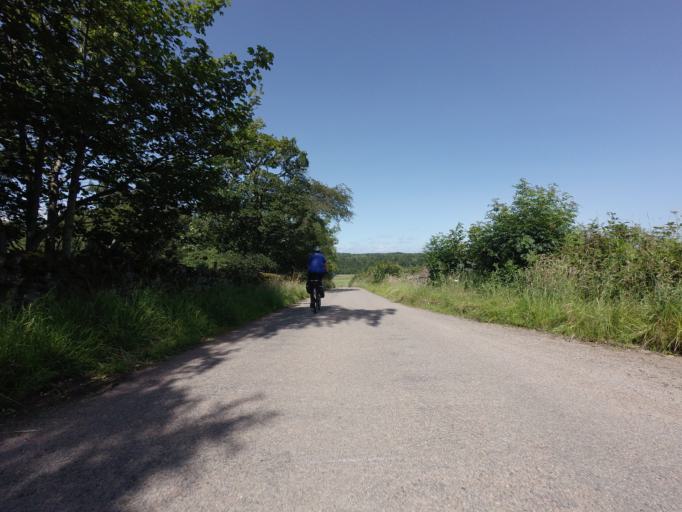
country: GB
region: Scotland
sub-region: Highland
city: Nairn
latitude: 57.5035
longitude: -3.9921
